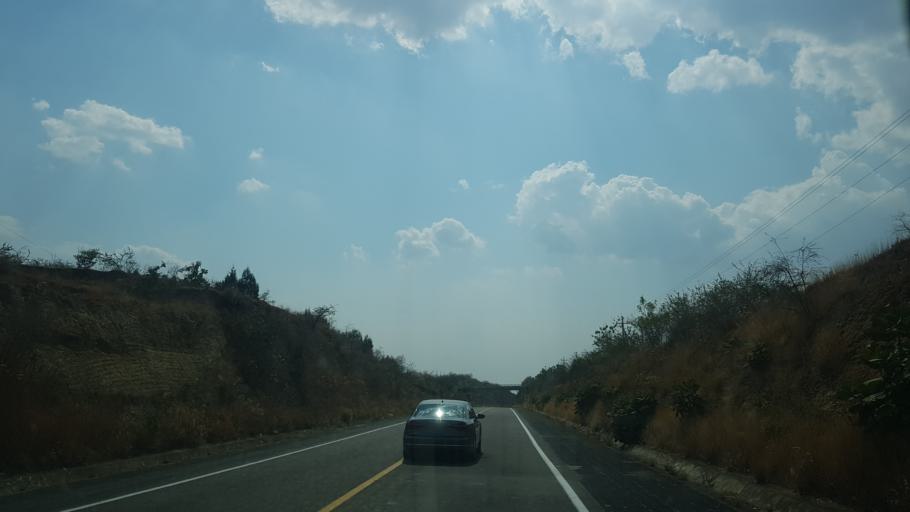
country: MX
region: Puebla
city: San Juan Amecac
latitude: 18.8160
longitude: -98.6678
